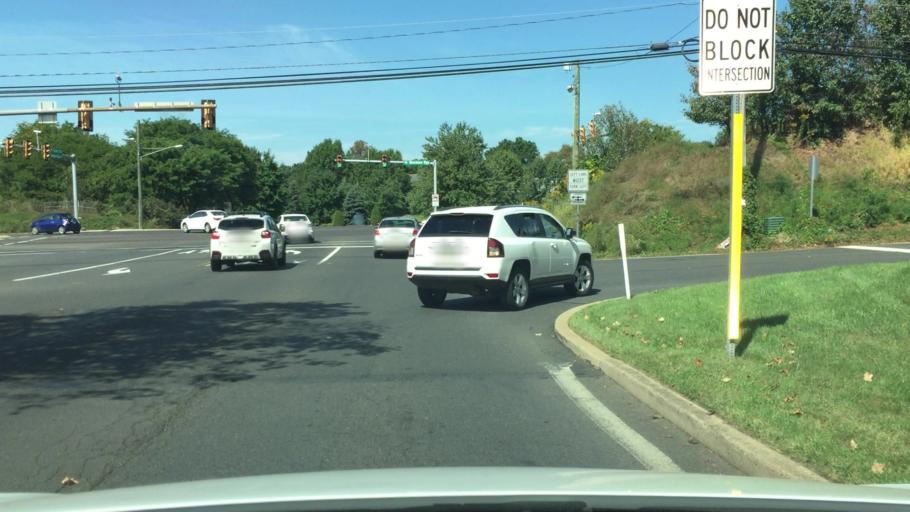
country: US
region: Pennsylvania
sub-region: Bucks County
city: Newtown
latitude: 40.2181
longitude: -74.9259
